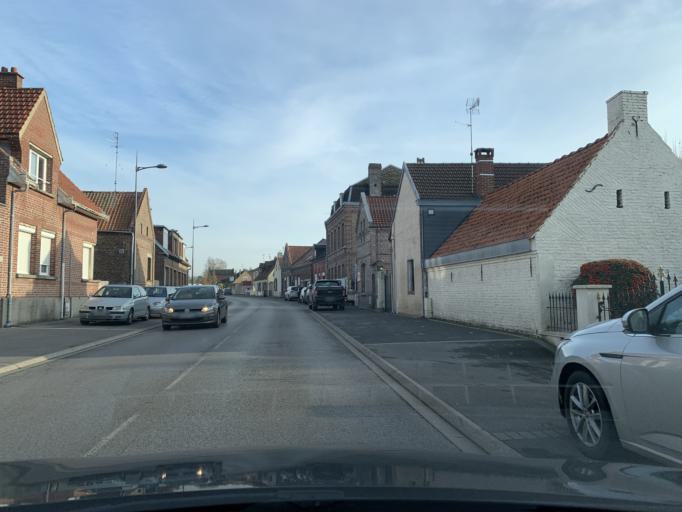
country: FR
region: Nord-Pas-de-Calais
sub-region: Departement du Nord
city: Cambrai
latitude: 50.1633
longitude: 3.2526
